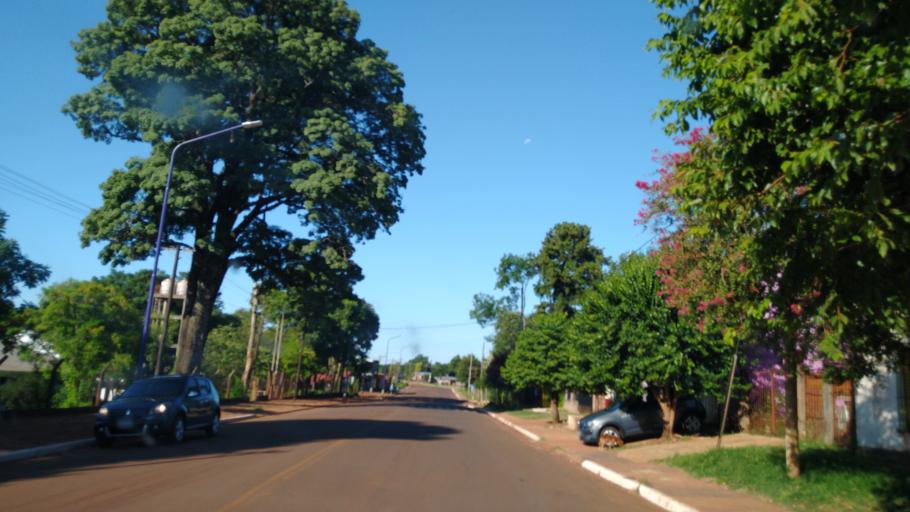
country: AR
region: Misiones
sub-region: Departamento de San Ignacio
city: San Ignacio
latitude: -27.2511
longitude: -55.5316
